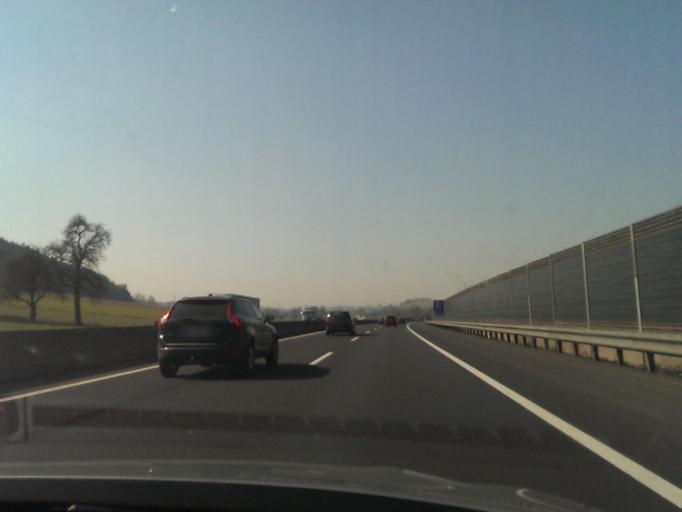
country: AT
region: Upper Austria
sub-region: Wels-Land
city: Pennewang
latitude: 48.1774
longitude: 13.8815
